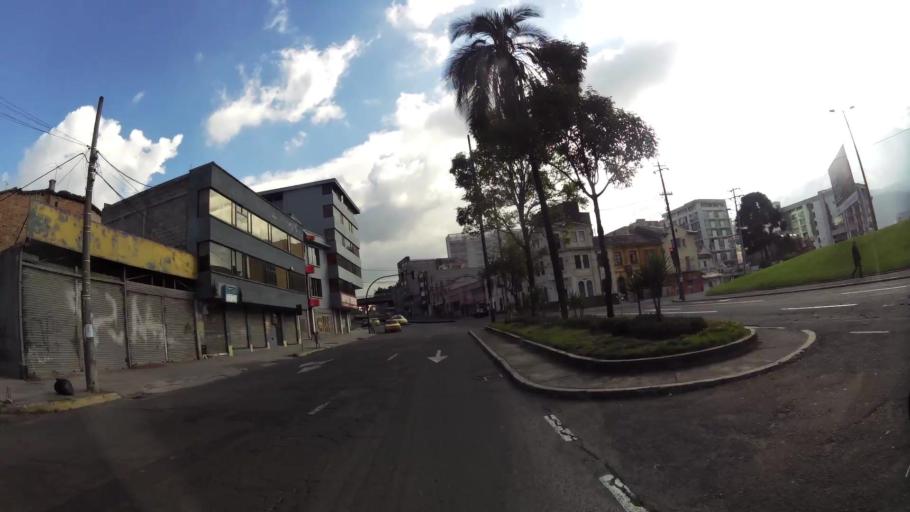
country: EC
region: Pichincha
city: Quito
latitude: -0.2122
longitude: -78.4965
